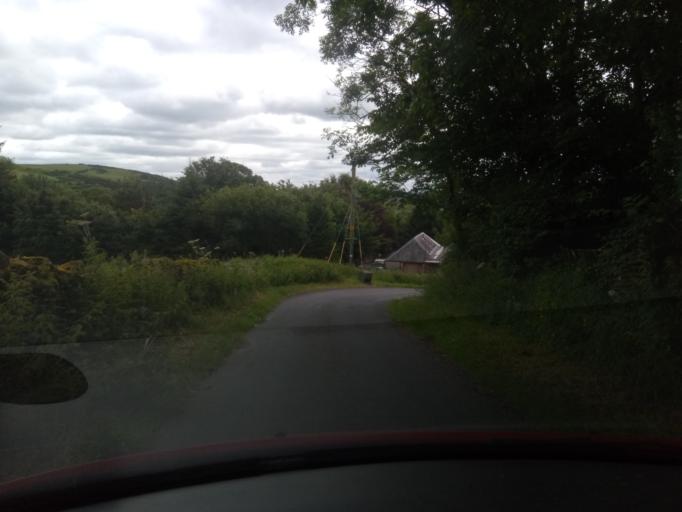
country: GB
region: Scotland
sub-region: The Scottish Borders
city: Hawick
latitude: 55.4321
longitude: -2.8215
